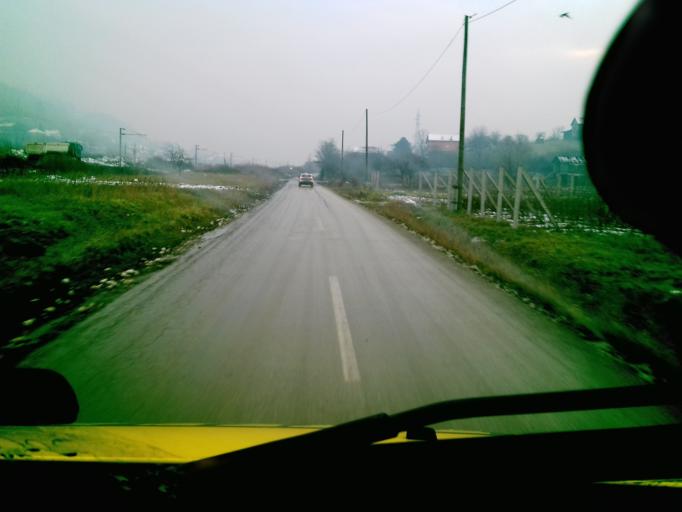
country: BA
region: Federation of Bosnia and Herzegovina
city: Zenica
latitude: 44.2467
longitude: 17.8966
